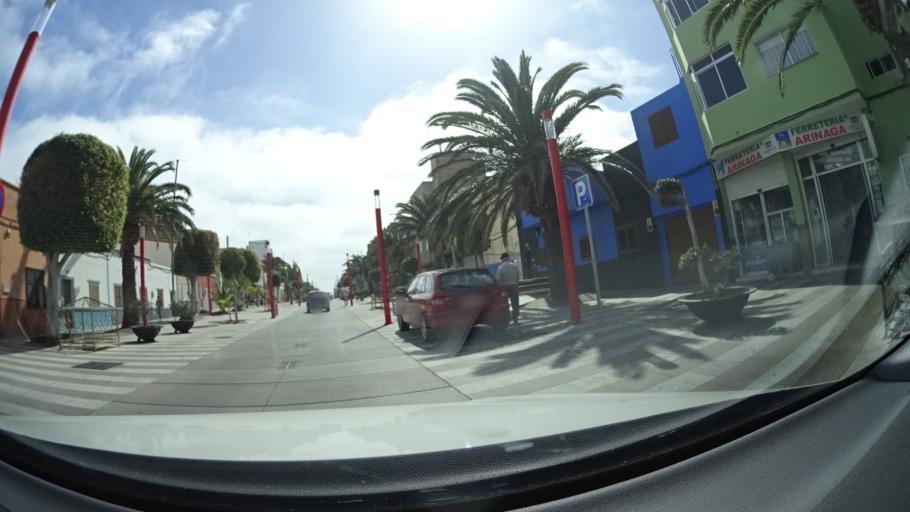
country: ES
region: Canary Islands
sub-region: Provincia de Las Palmas
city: Cruce de Arinaga
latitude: 27.8579
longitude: -15.3965
